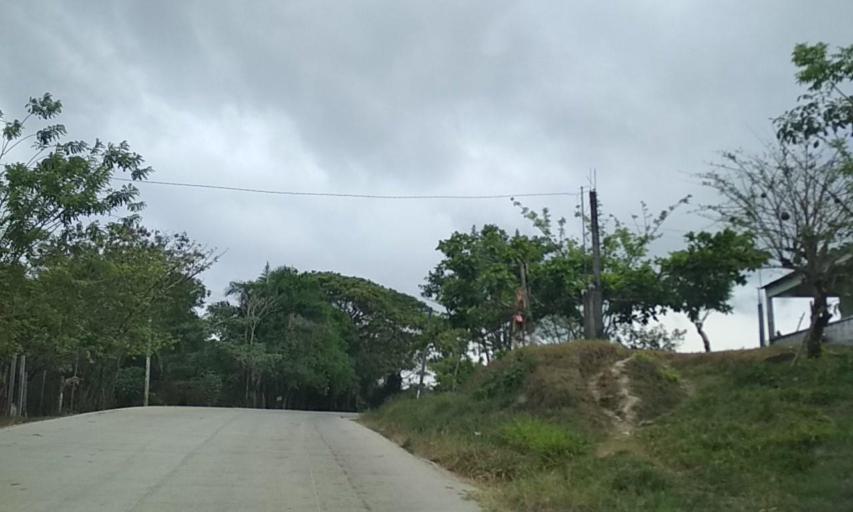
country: MX
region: Tabasco
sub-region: Huimanguillo
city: Francisco Rueda
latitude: 17.6536
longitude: -94.0923
